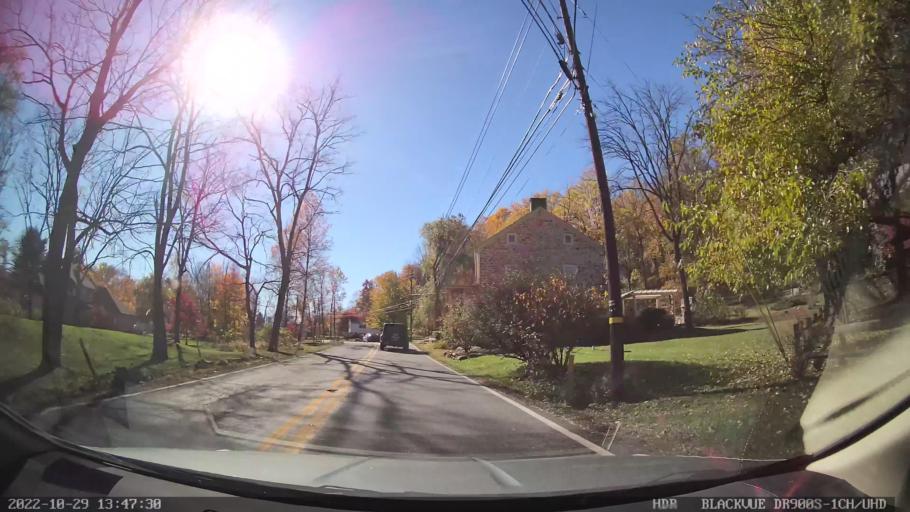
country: US
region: Pennsylvania
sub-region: Lehigh County
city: Emmaus
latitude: 40.5549
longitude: -75.4449
